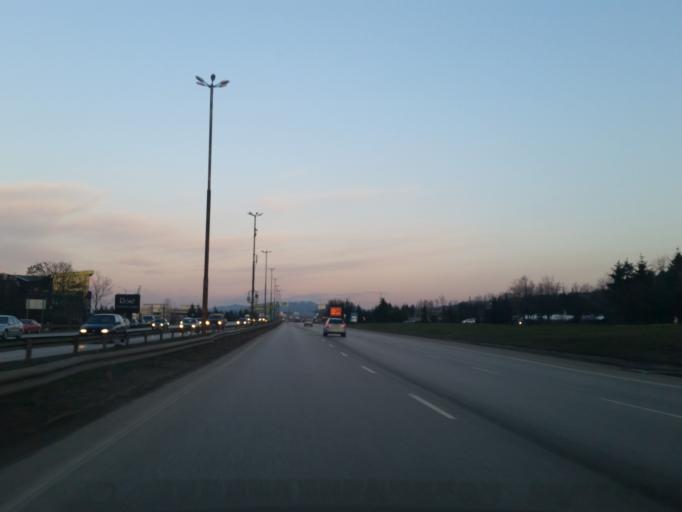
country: BG
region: Sofia-Capital
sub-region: Stolichna Obshtina
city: Sofia
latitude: 42.6555
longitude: 23.2779
